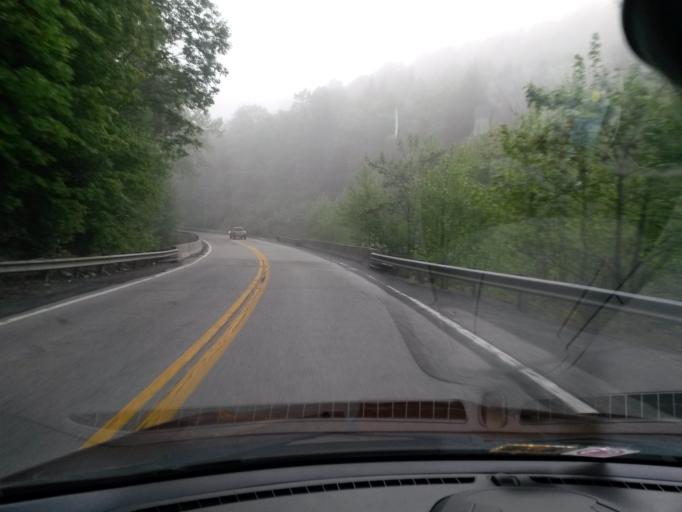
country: US
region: West Virginia
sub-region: McDowell County
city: Welch
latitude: 37.5020
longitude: -81.5438
